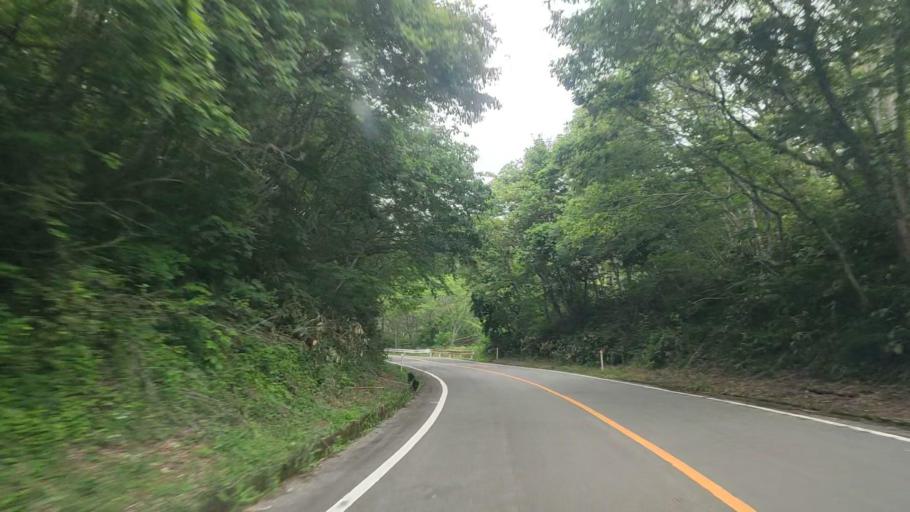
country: JP
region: Tottori
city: Kurayoshi
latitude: 35.3032
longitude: 133.6226
